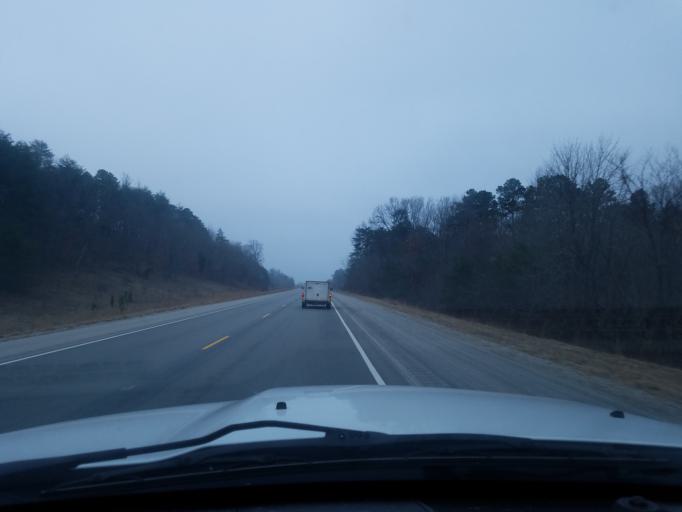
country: US
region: Indiana
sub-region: Perry County
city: Tell City
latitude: 38.0724
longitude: -86.6176
